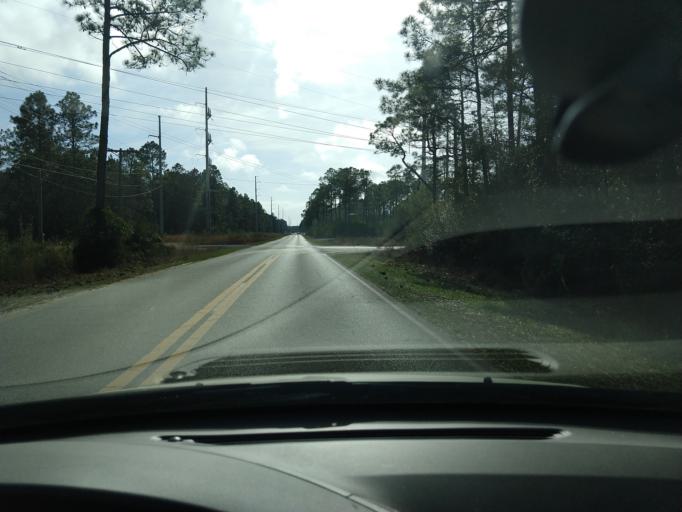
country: US
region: Florida
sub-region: Walton County
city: Seaside
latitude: 30.3616
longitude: -86.1250
